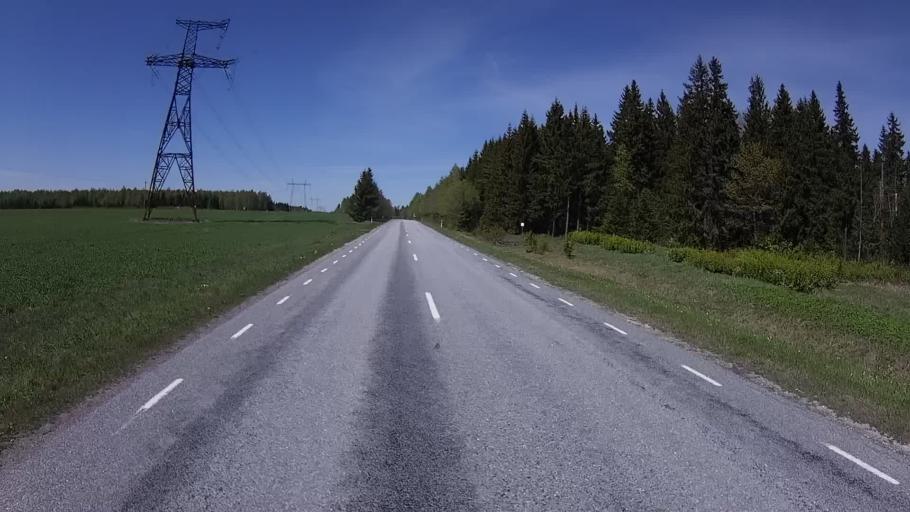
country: EE
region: Raplamaa
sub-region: Kehtna vald
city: Kehtna
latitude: 59.0405
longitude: 25.0364
